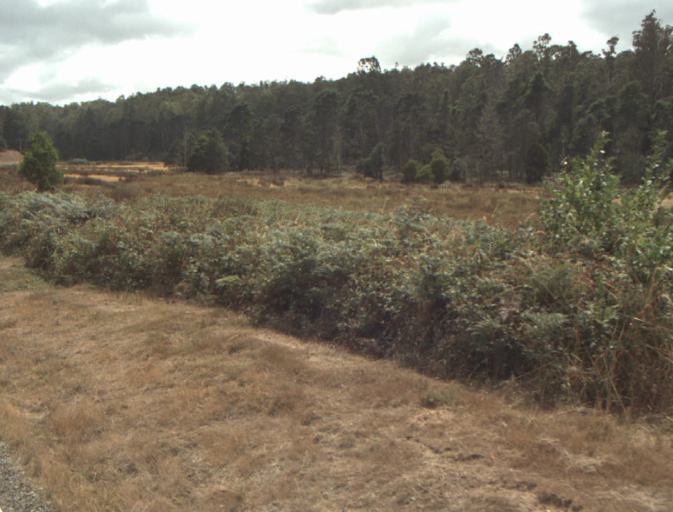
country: AU
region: Tasmania
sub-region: Dorset
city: Bridport
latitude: -41.1900
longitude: 147.2619
